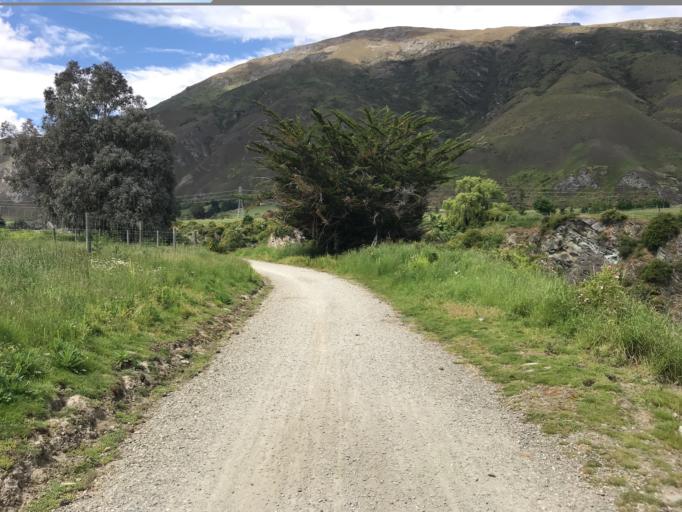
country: NZ
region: Otago
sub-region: Queenstown-Lakes District
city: Arrowtown
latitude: -45.0018
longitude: 168.8752
